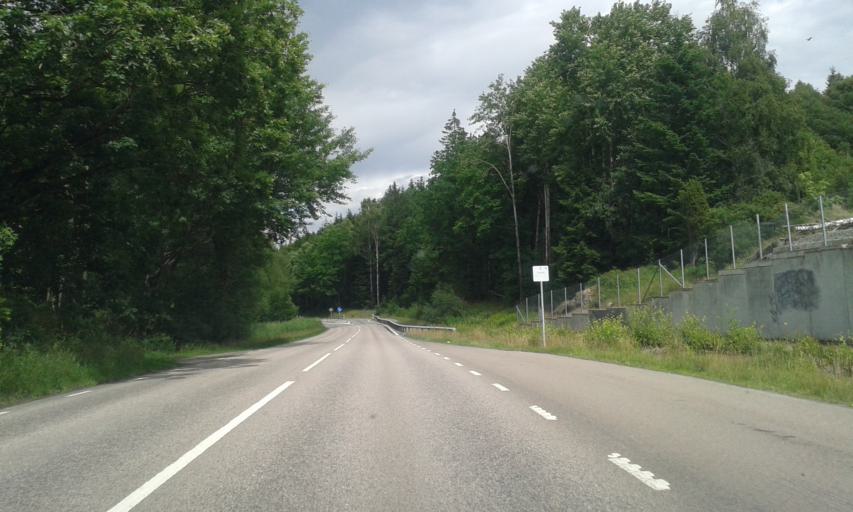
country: SE
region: Vaestra Goetaland
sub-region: Kungalvs Kommun
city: Diserod
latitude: 57.8959
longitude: 12.0039
